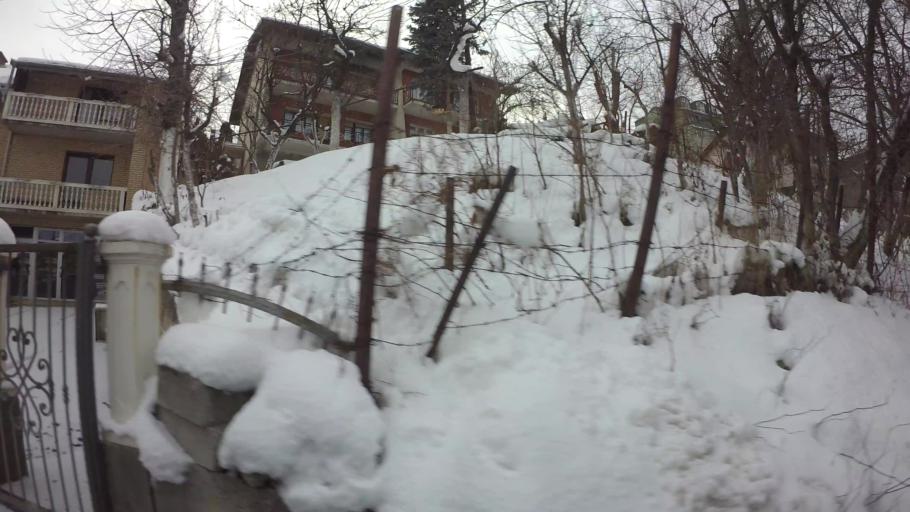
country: BA
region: Federation of Bosnia and Herzegovina
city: Kobilja Glava
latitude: 43.8650
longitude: 18.3968
